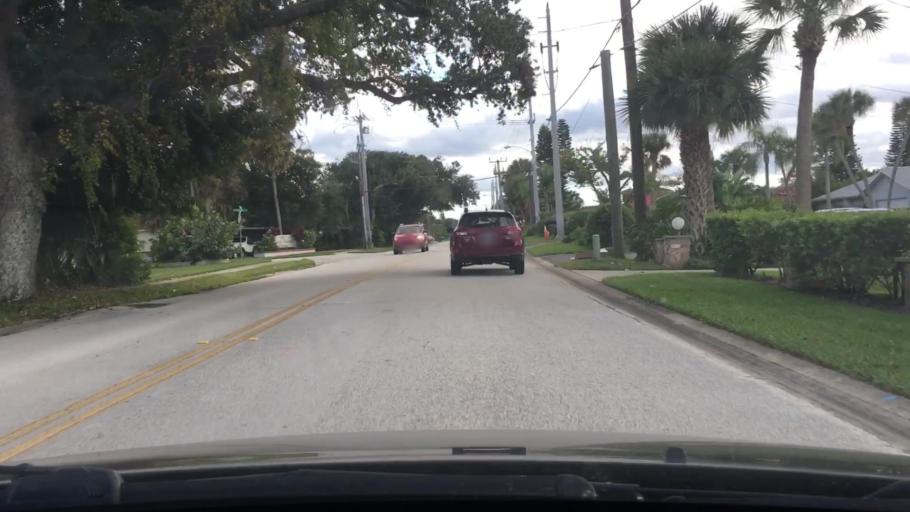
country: US
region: Florida
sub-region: Volusia County
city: Ormond Beach
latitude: 29.2724
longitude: -81.0393
